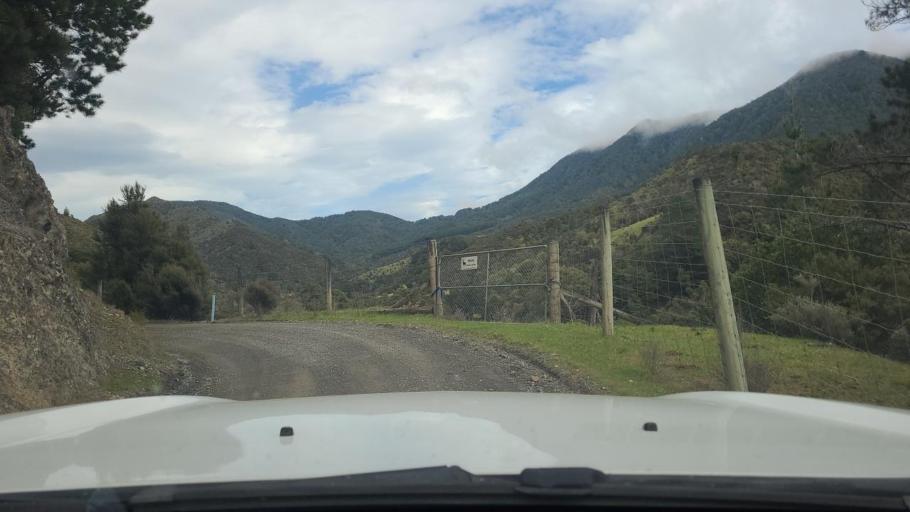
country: NZ
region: Wellington
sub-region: South Wairarapa District
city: Waipawa
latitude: -41.3879
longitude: 175.3710
